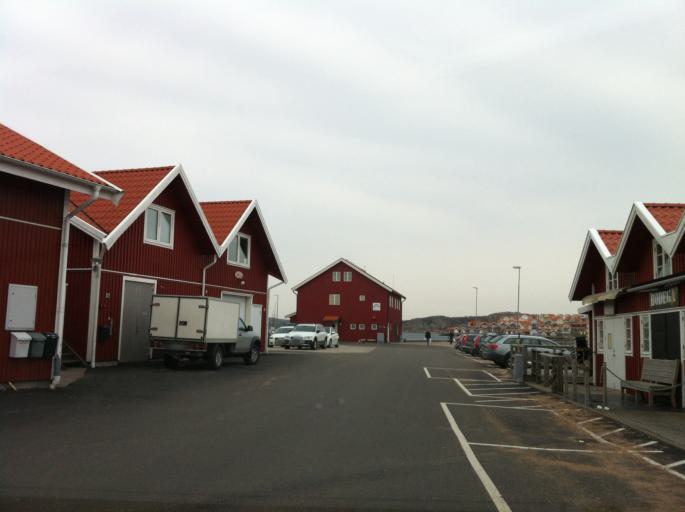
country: SE
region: Vaestra Goetaland
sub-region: Tjorns Kommun
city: Myggenas
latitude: 58.1412
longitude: 11.7117
